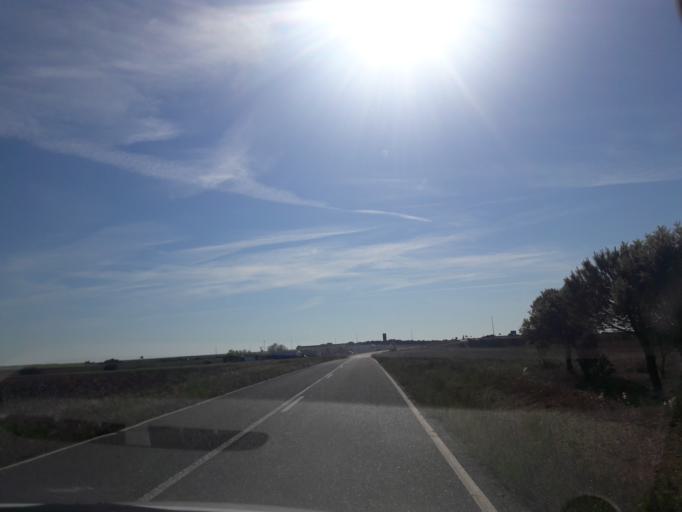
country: ES
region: Castille and Leon
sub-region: Provincia de Salamanca
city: Aldeanueva de Figueroa
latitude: 41.1375
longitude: -5.4927
